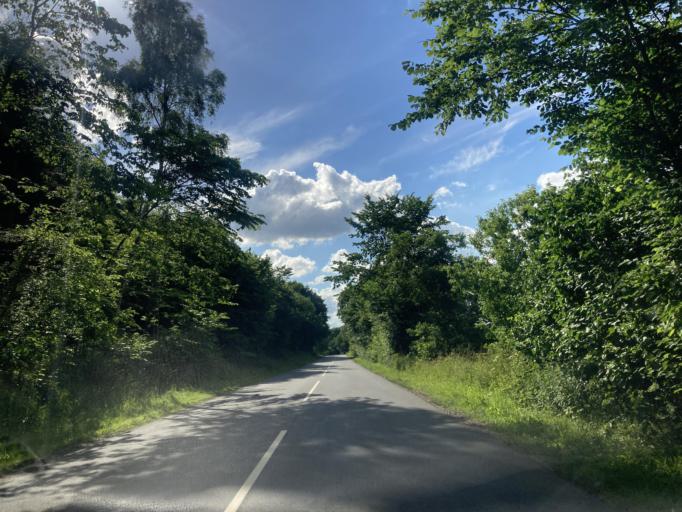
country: DK
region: South Denmark
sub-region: Kolding Kommune
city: Kolding
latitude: 55.4842
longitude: 9.4056
